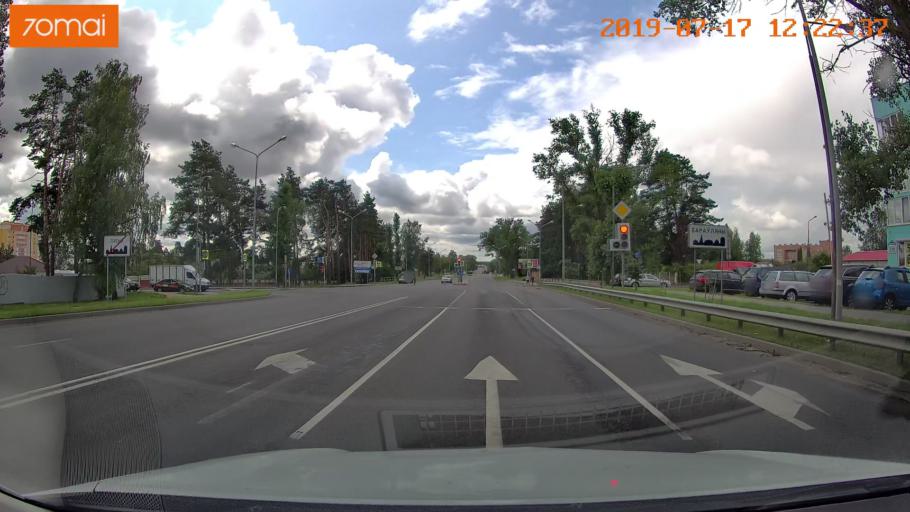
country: BY
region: Minsk
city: Borovlyany
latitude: 54.0002
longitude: 27.6767
